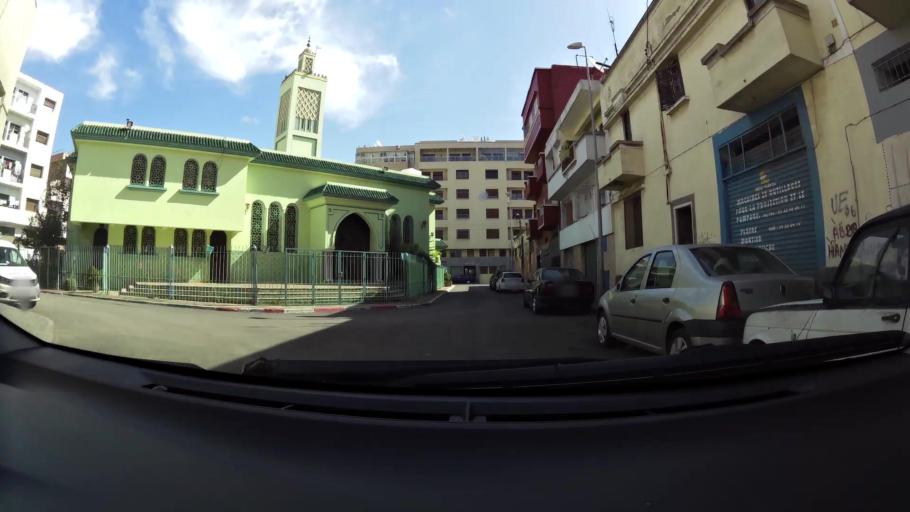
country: MA
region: Grand Casablanca
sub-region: Casablanca
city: Casablanca
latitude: 33.5896
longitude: -7.5801
